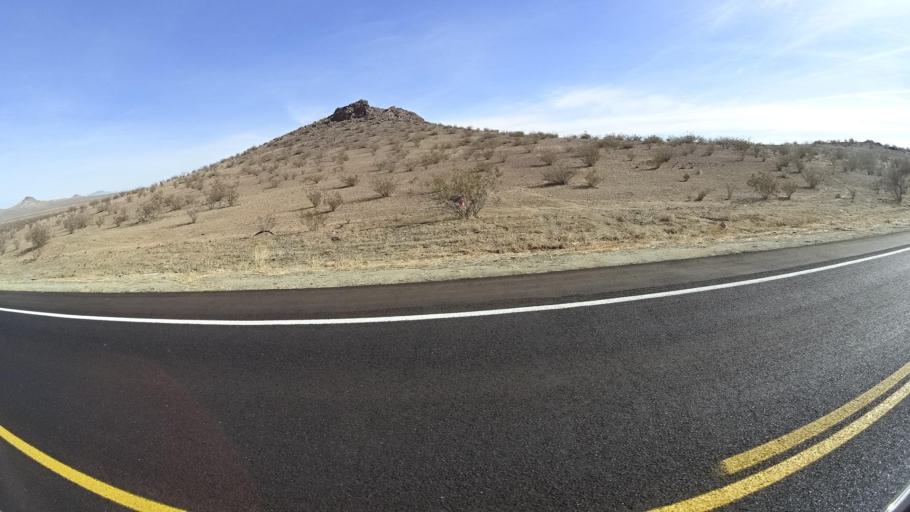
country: US
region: California
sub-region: Kern County
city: California City
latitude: 35.0630
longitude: -117.9177
